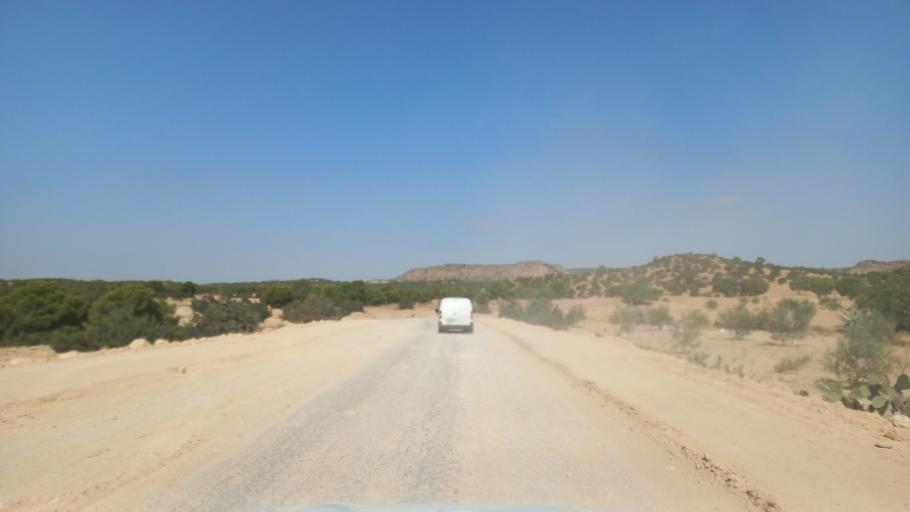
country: TN
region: Al Qasrayn
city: Sbiba
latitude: 35.4064
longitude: 8.9875
